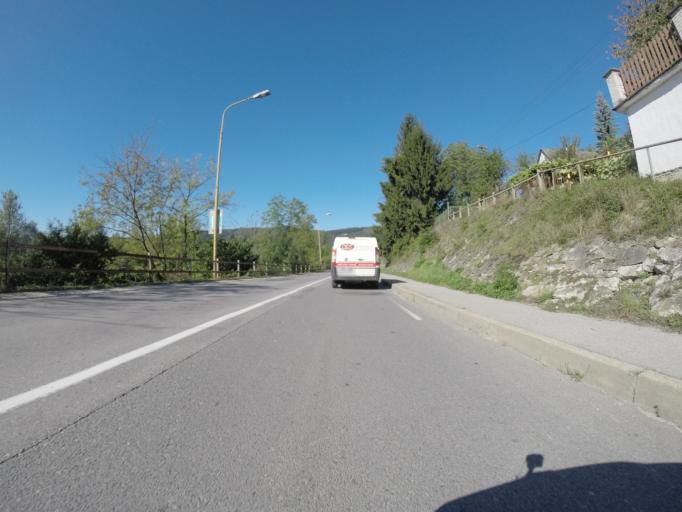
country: SK
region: Trenciansky
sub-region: Okres Povazska Bystrica
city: Povazska Bystrica
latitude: 49.1254
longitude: 18.4371
